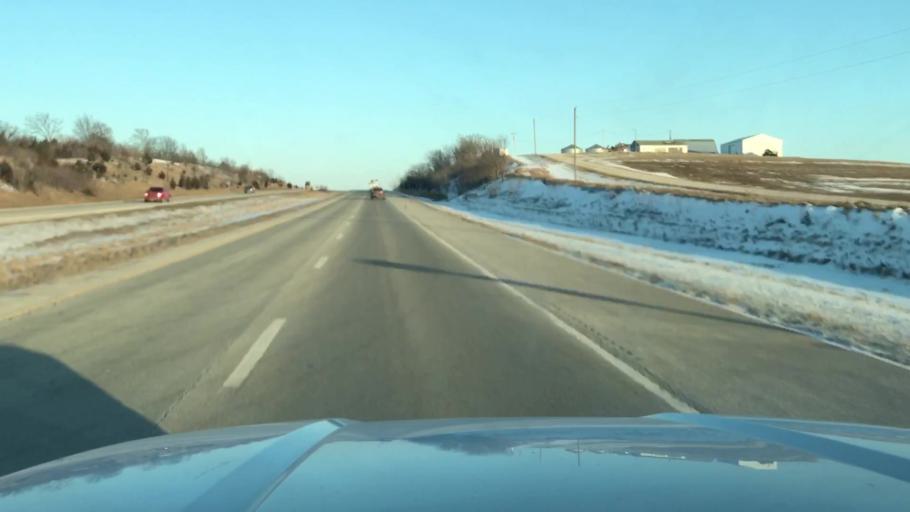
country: US
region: Missouri
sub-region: Buchanan County
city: Saint Joseph
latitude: 39.7475
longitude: -94.7115
